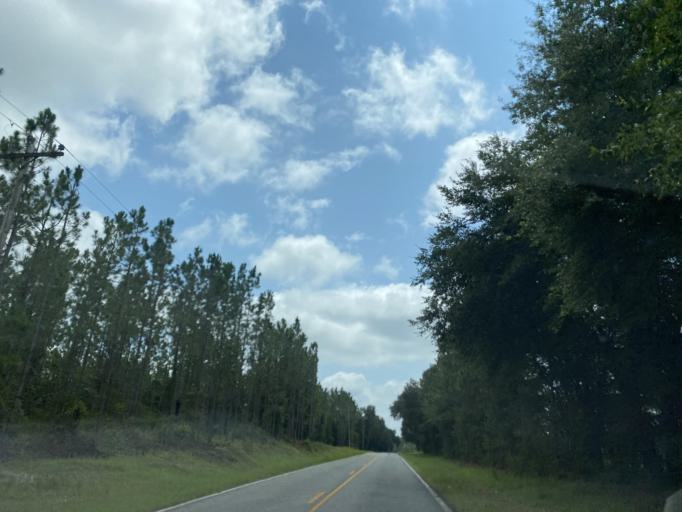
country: US
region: Georgia
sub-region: Wheeler County
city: Alamo
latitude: 32.1208
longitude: -82.7881
